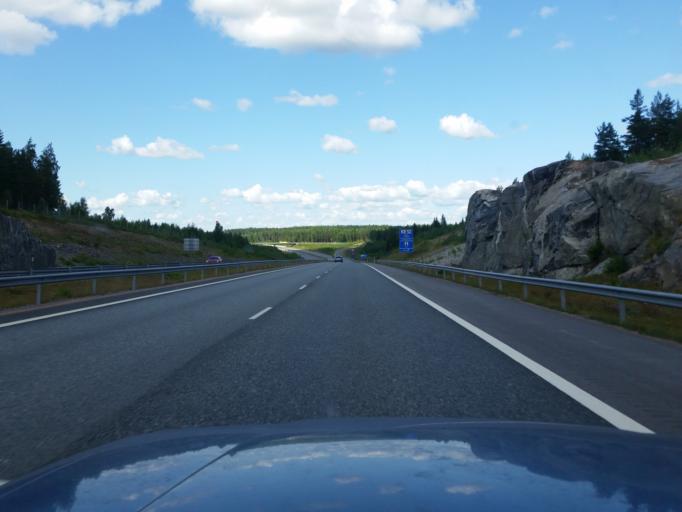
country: FI
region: Varsinais-Suomi
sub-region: Salo
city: Suomusjaervi
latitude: 60.3765
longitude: 23.6368
